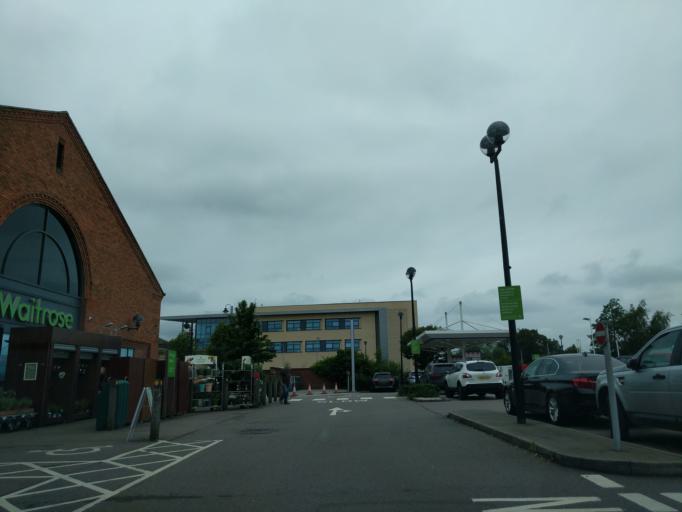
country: GB
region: England
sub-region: Nottinghamshire
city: Newark on Trent
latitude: 53.0803
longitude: -0.8117
